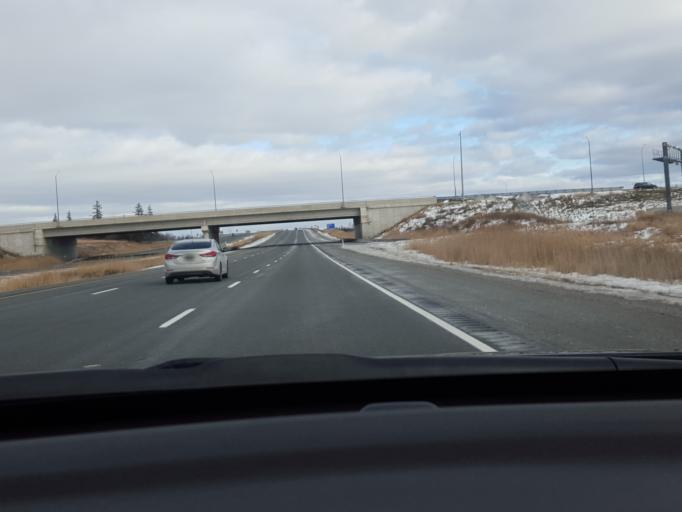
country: CA
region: Ontario
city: Markham
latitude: 43.8740
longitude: -79.2159
